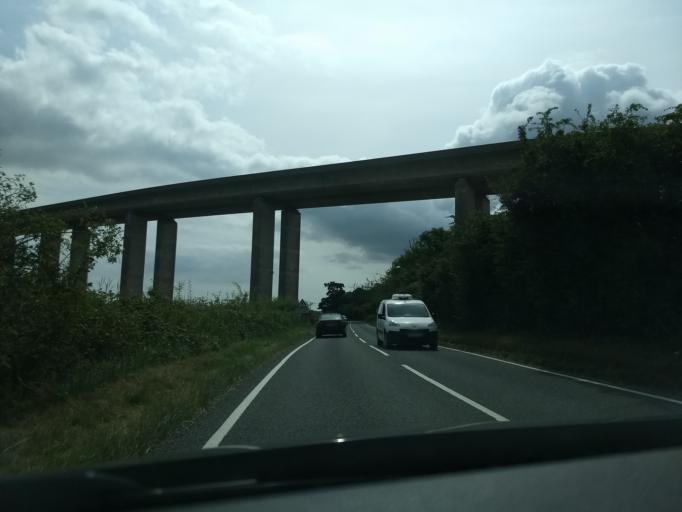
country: GB
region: England
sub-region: Suffolk
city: Ipswich
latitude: 52.0279
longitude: 1.1569
